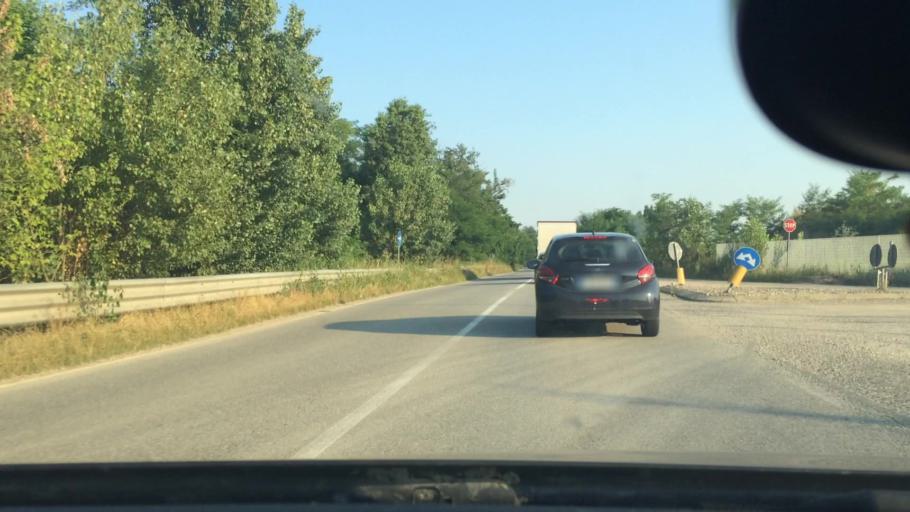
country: IT
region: Lombardy
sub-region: Citta metropolitana di Milano
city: Mantegazza
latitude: 45.5153
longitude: 8.9610
